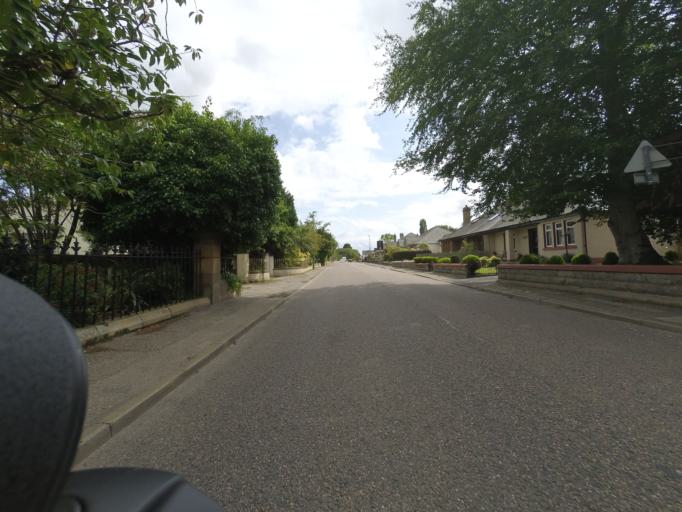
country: GB
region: Scotland
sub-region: Highland
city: Tain
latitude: 57.8081
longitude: -4.0502
